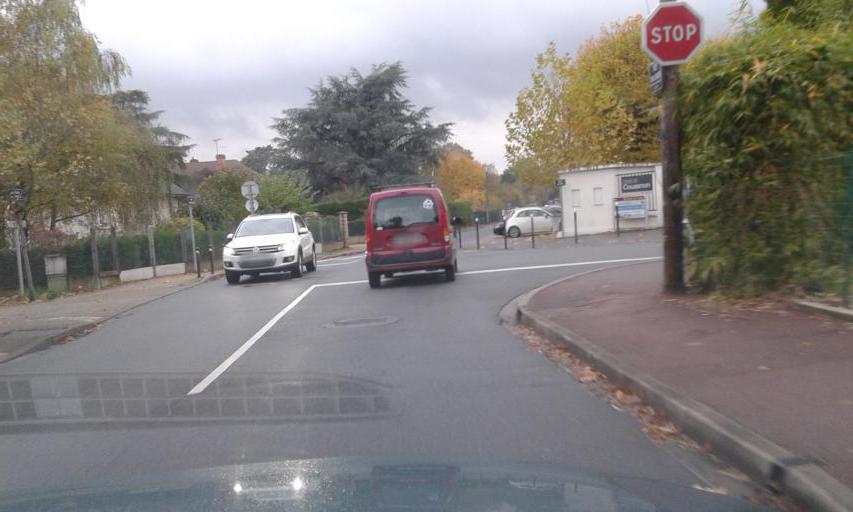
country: FR
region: Centre
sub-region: Departement du Loiret
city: Olivet
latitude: 47.8697
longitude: 1.8978
